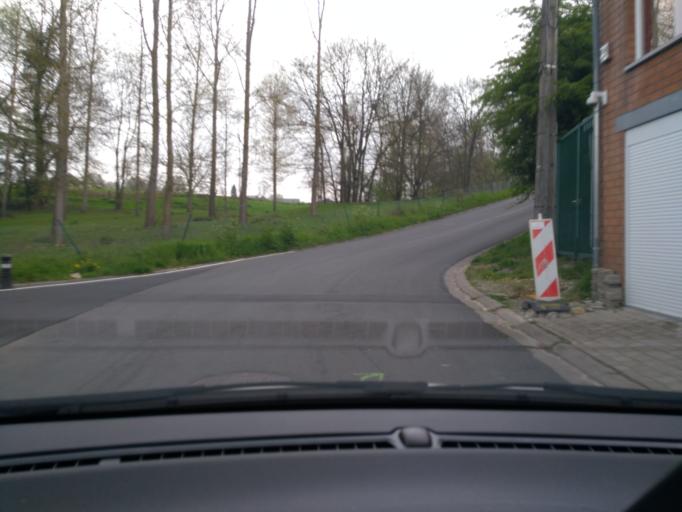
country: BE
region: Wallonia
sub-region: Province de Namur
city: Namur
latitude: 50.4582
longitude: 4.8150
